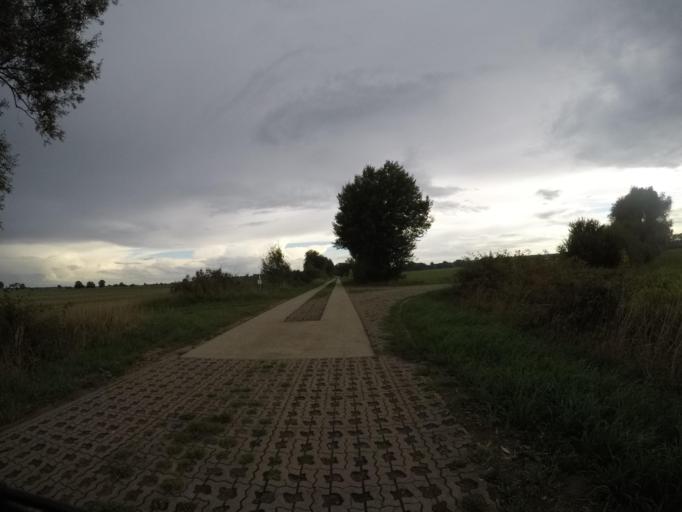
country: DE
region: Lower Saxony
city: Neu Darchau
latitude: 53.2600
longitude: 10.8802
